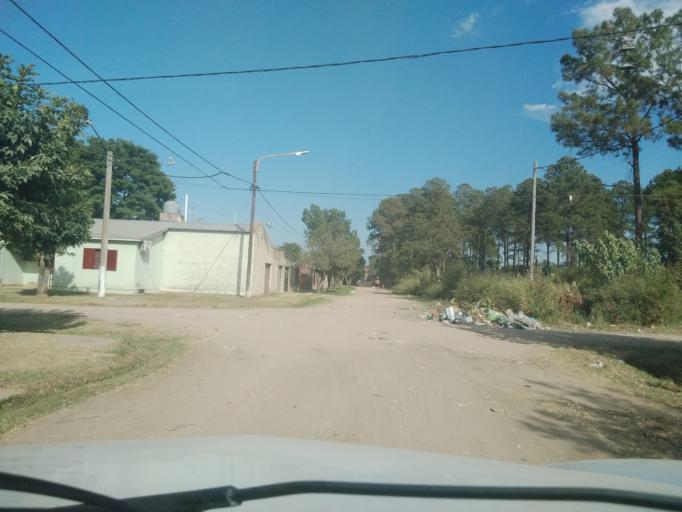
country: AR
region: Corrientes
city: Corrientes
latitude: -27.5092
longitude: -58.8021
